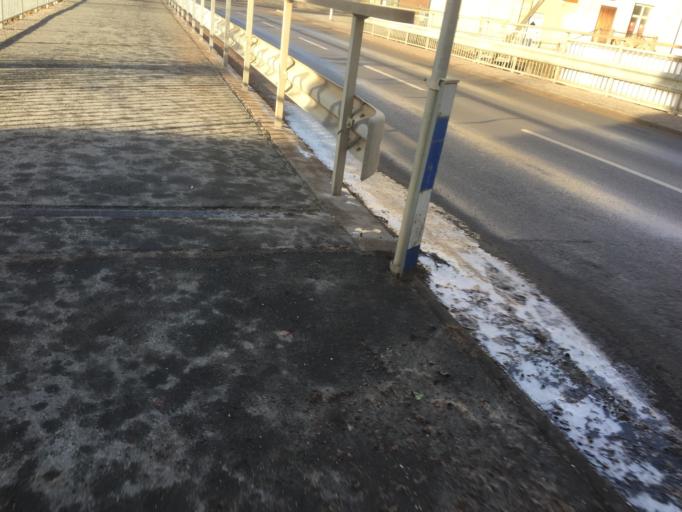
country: SE
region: Joenkoeping
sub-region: Aneby Kommun
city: Aneby
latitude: 57.8389
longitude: 14.8141
